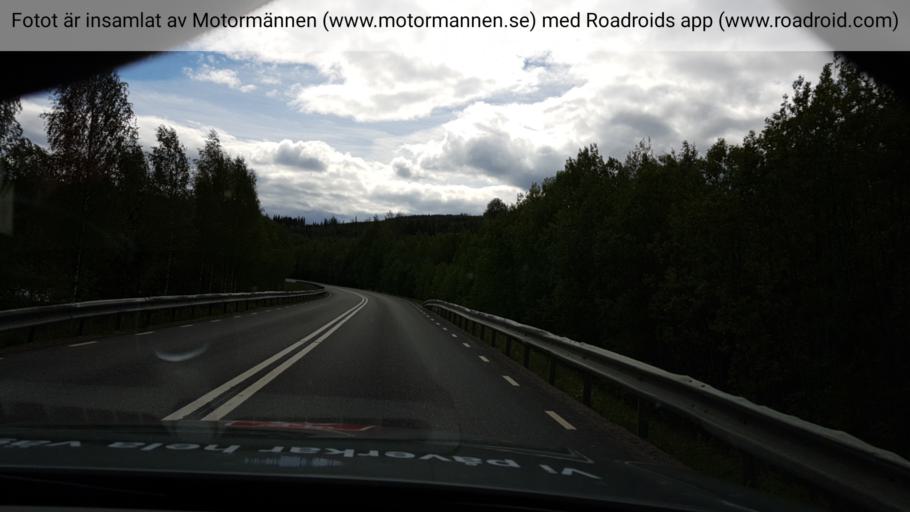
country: SE
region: Jaemtland
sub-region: Stroemsunds Kommun
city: Stroemsund
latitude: 64.0950
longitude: 15.5747
